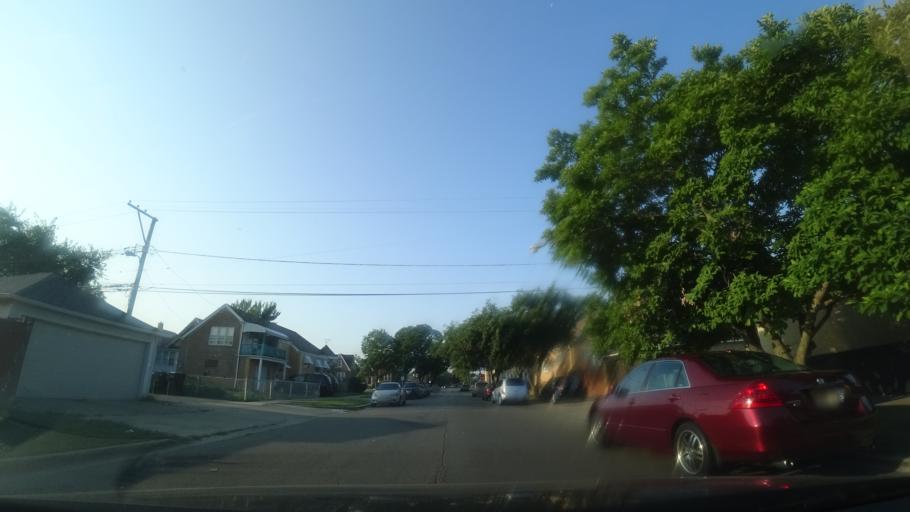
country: US
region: Illinois
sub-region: Cook County
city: Elmwood Park
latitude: 41.9400
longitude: -87.7713
